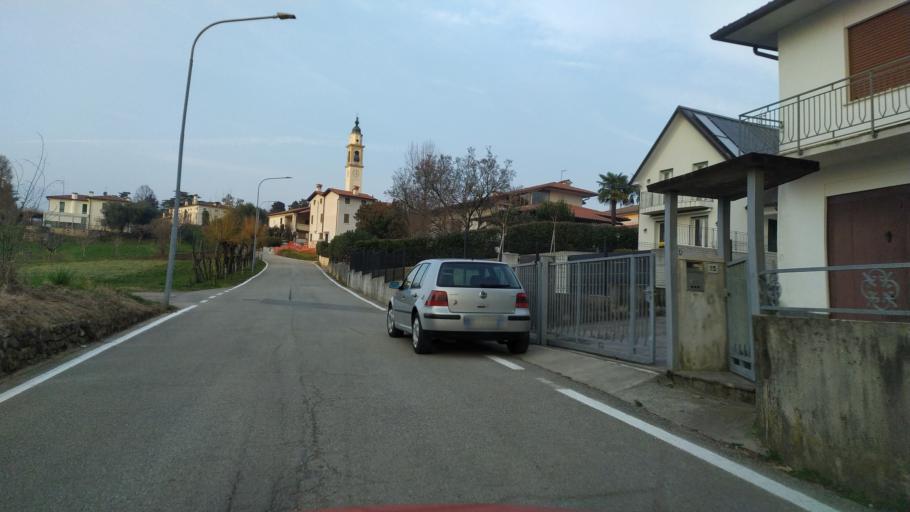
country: IT
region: Veneto
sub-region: Provincia di Vicenza
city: Sarcedo
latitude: 45.7052
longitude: 11.5260
